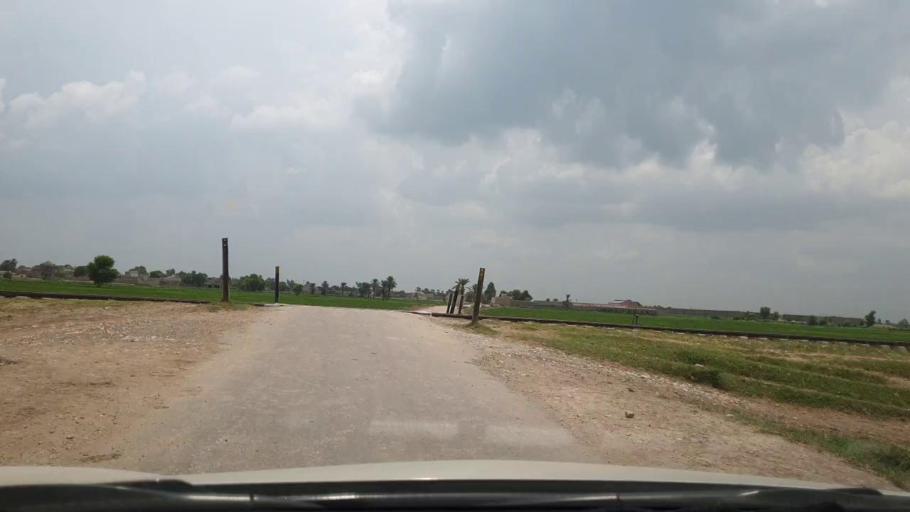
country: PK
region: Sindh
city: Goth Garelo
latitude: 27.4249
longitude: 68.1096
